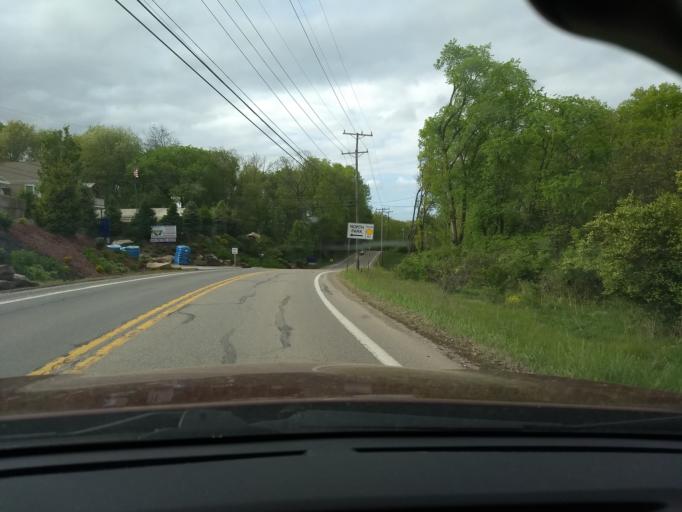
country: US
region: Pennsylvania
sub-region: Allegheny County
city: Russellton
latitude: 40.5986
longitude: -79.8893
